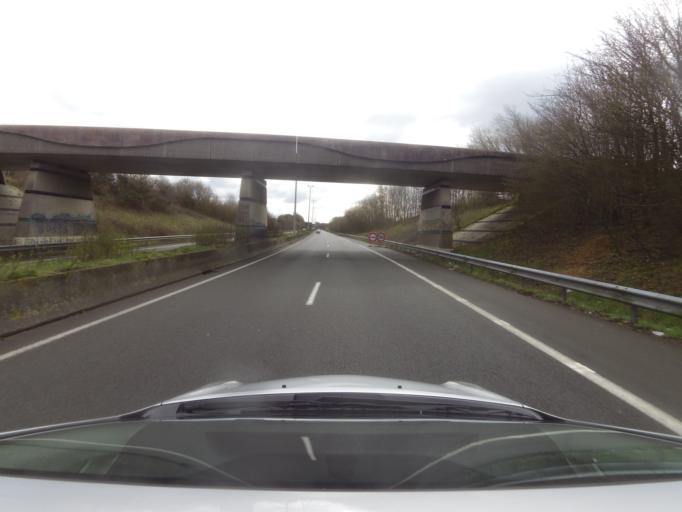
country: FR
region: Nord-Pas-de-Calais
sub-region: Departement du Pas-de-Calais
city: Saint-Martin-Boulogne
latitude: 50.7367
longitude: 1.6342
